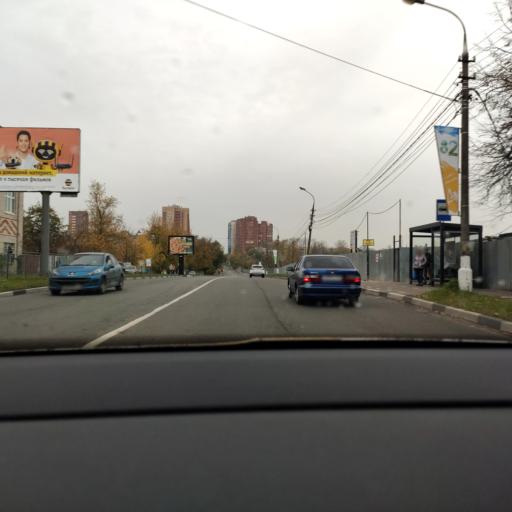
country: RU
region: Moskovskaya
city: Ivanteyevka
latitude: 55.9717
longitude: 37.9226
